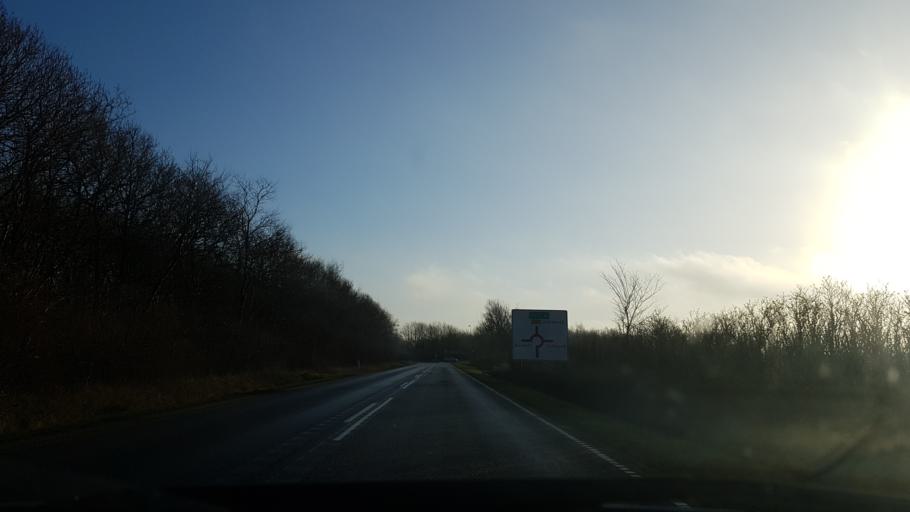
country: DK
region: South Denmark
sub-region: Haderslev Kommune
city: Vojens
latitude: 55.2007
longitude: 9.1954
